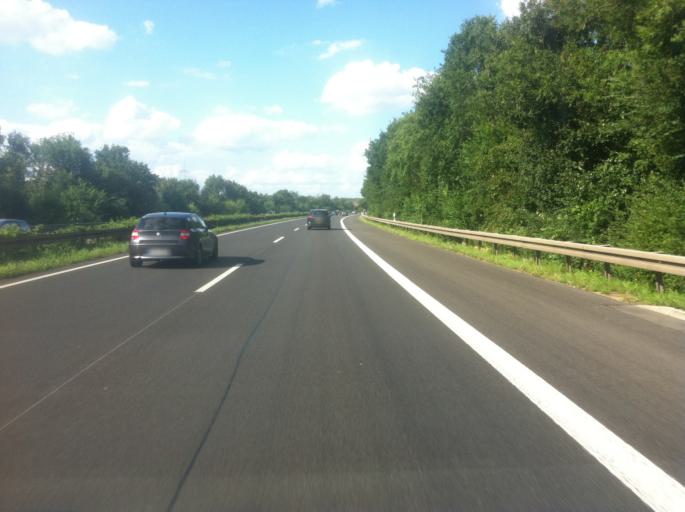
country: DE
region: North Rhine-Westphalia
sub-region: Regierungsbezirk Koln
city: Erftstadt
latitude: 50.8256
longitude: 6.7858
